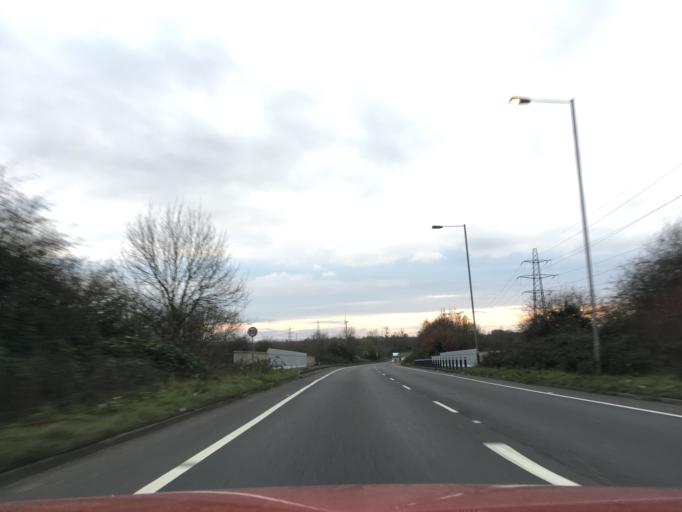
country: GB
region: Wales
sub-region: Monmouthshire
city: Magor
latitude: 51.5793
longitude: -2.8449
